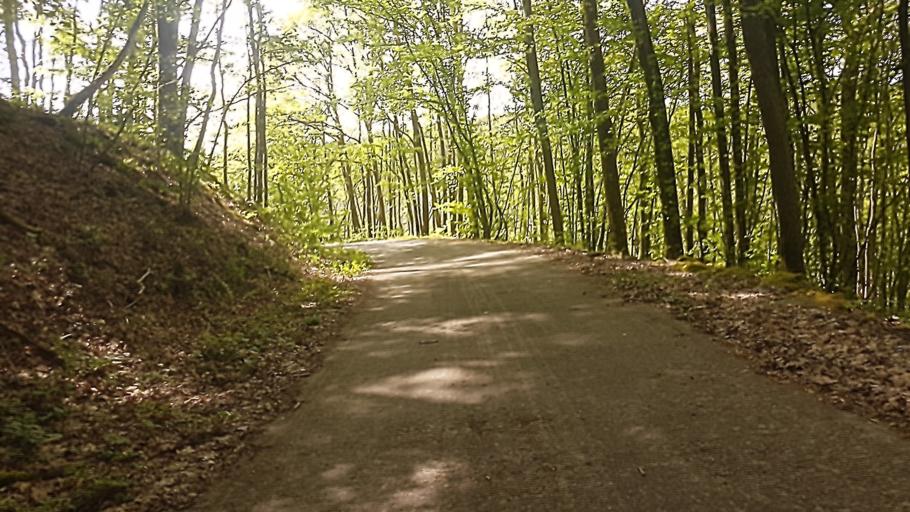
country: BE
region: Wallonia
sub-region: Province de Namur
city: Couvin
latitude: 50.0413
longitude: 4.5935
